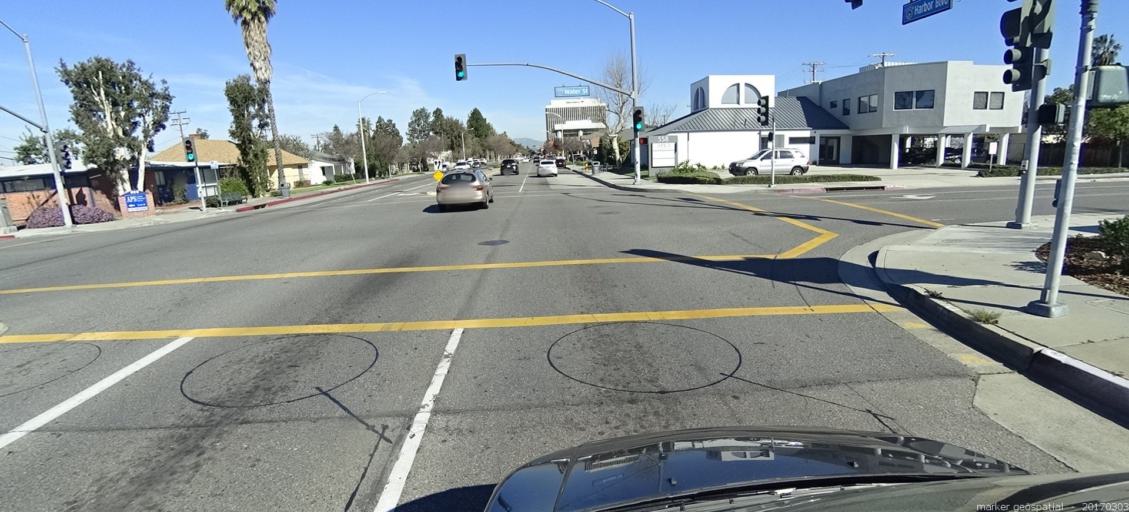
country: US
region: California
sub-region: Orange County
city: Anaheim
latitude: 33.8274
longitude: -117.9173
